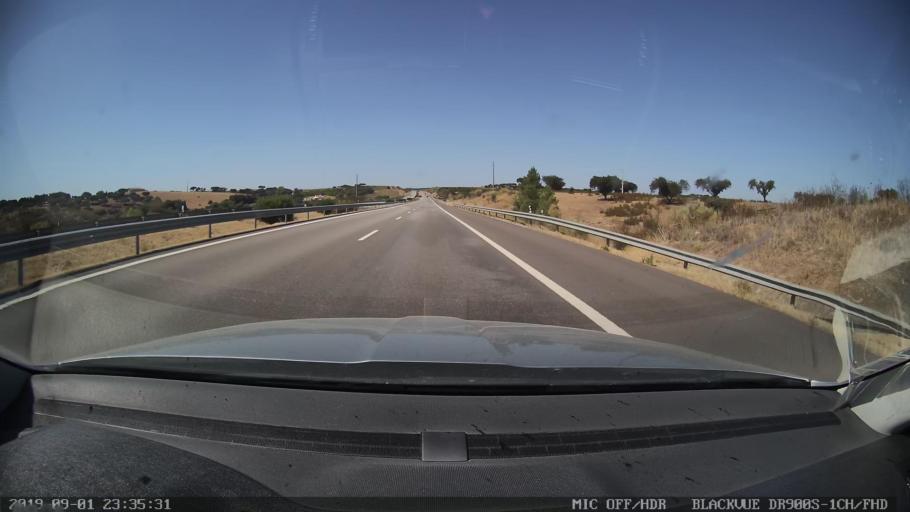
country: PT
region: Evora
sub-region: Vila Vicosa
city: Vila Vicosa
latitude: 38.8446
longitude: -7.3948
